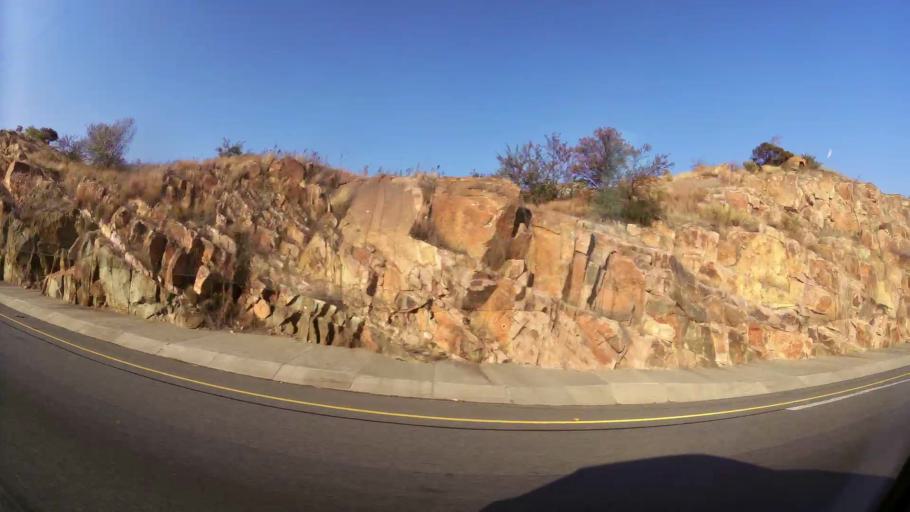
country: ZA
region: Gauteng
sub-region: Ekurhuleni Metropolitan Municipality
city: Germiston
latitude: -26.2505
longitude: 28.1228
